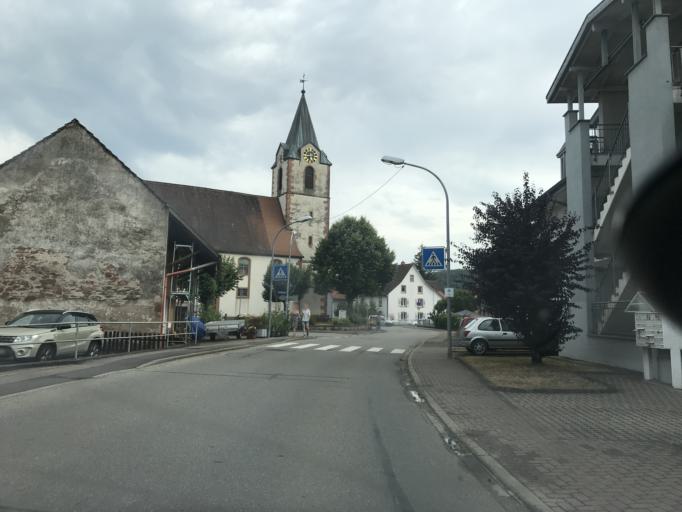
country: DE
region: Baden-Wuerttemberg
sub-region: Freiburg Region
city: Steinen
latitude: 47.6457
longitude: 7.7392
